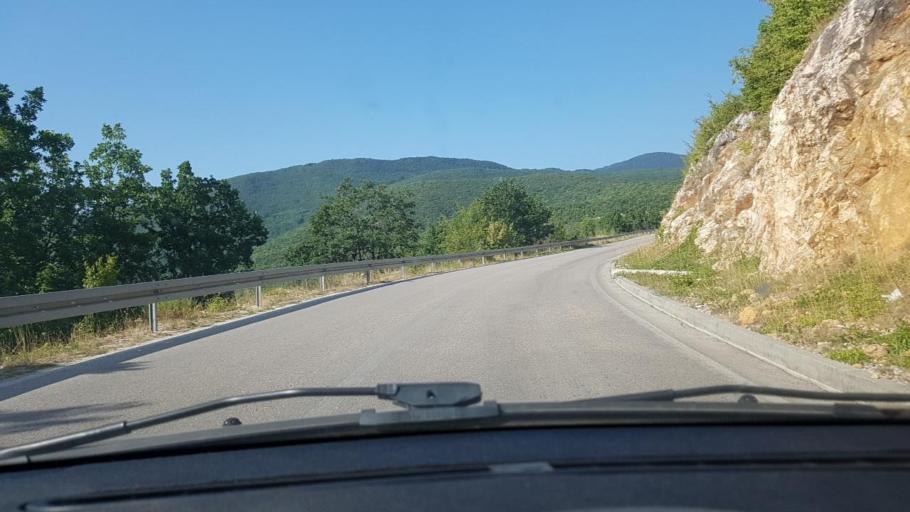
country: BA
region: Federation of Bosnia and Herzegovina
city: Rumboci
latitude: 43.8251
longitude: 17.4823
